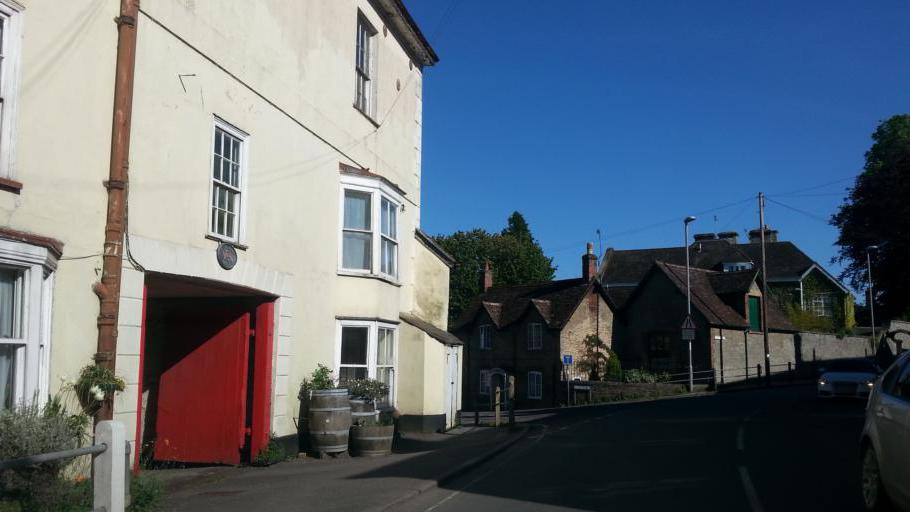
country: GB
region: England
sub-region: Dorset
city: Stalbridge
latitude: 50.9616
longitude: -2.3791
